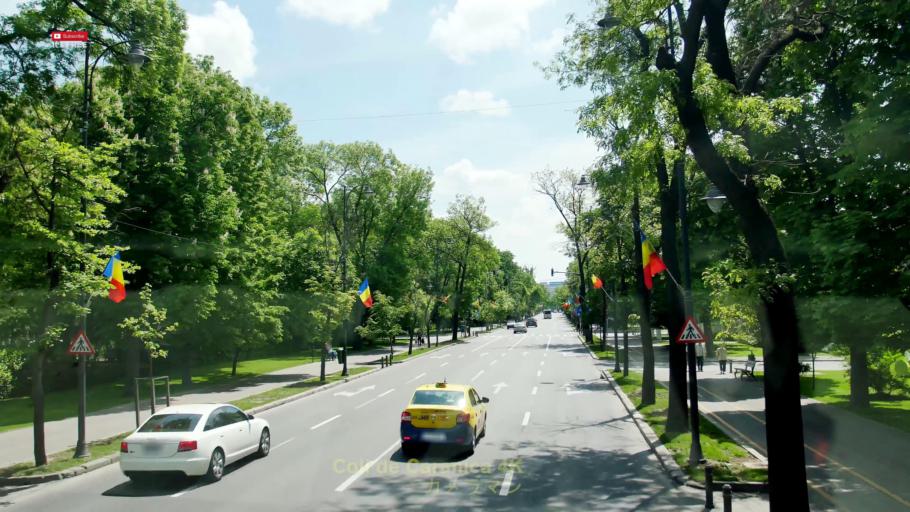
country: RO
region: Bucuresti
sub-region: Municipiul Bucuresti
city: Bucuresti
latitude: 44.4634
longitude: 26.0800
